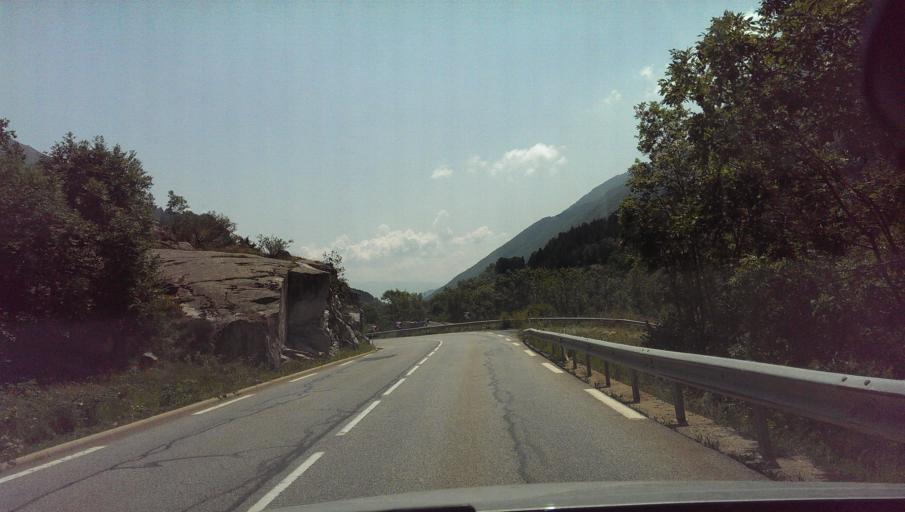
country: ES
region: Catalonia
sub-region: Provincia de Girona
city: Meranges
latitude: 42.5130
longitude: 1.8257
